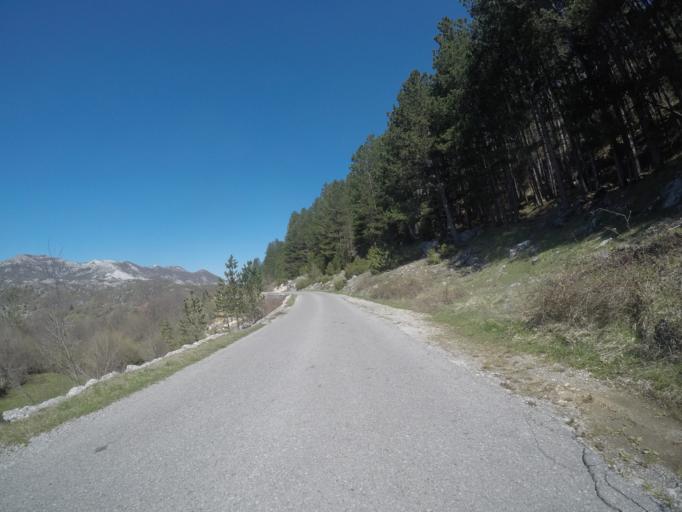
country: ME
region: Cetinje
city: Cetinje
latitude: 42.4608
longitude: 18.8657
